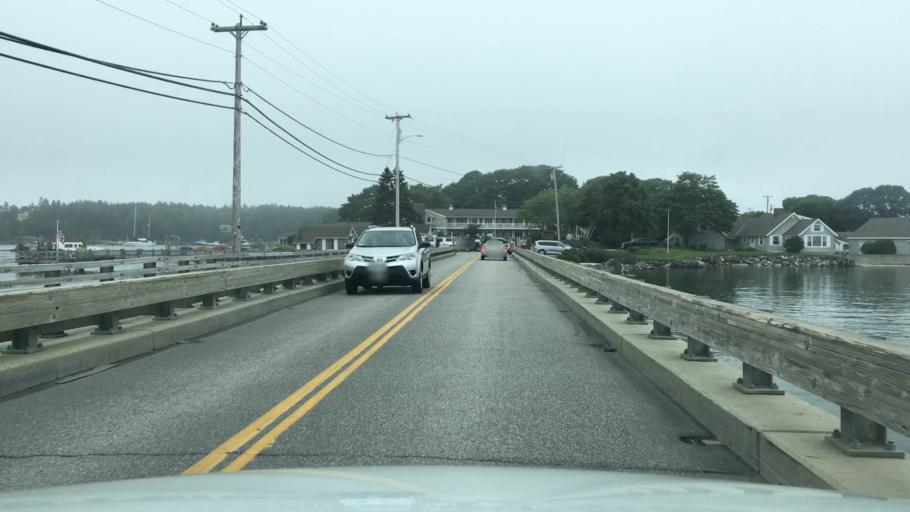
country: US
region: Maine
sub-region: Cumberland County
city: Harpswell Center
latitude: 43.7485
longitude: -69.9891
